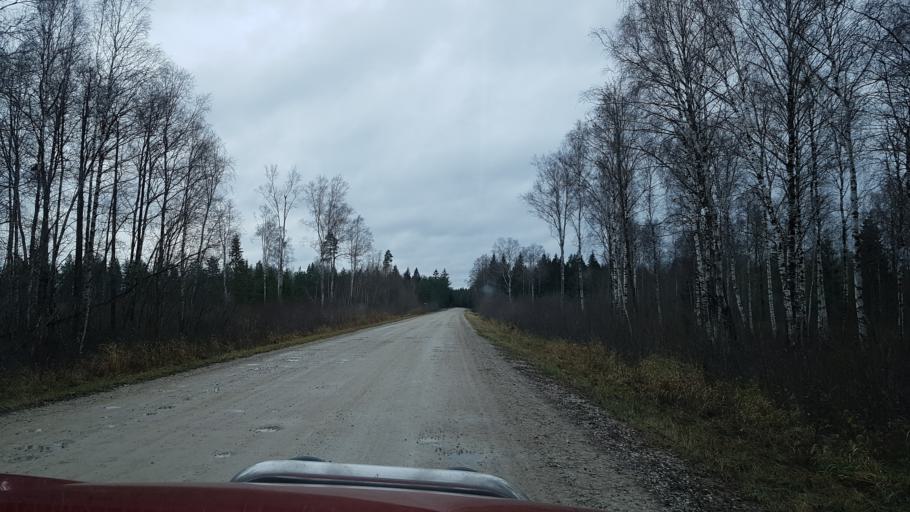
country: EE
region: Paernumaa
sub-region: Halinga vald
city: Parnu-Jaagupi
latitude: 58.5584
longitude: 24.4137
